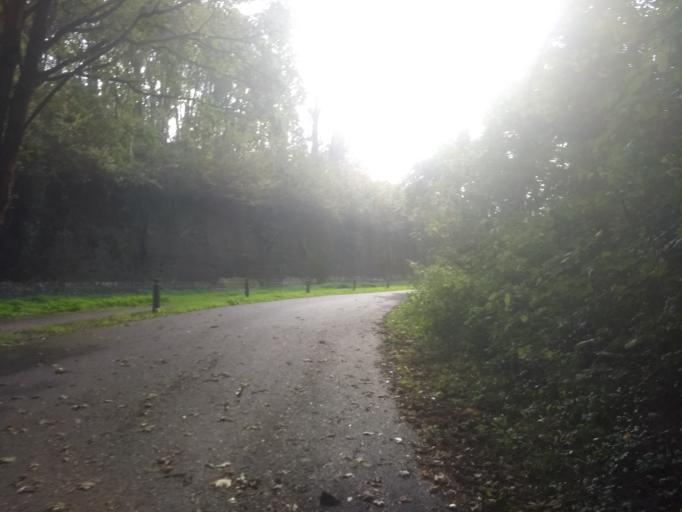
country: FR
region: Nord-Pas-de-Calais
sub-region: Departement du Pas-de-Calais
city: Achicourt
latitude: 50.2832
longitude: 2.7562
